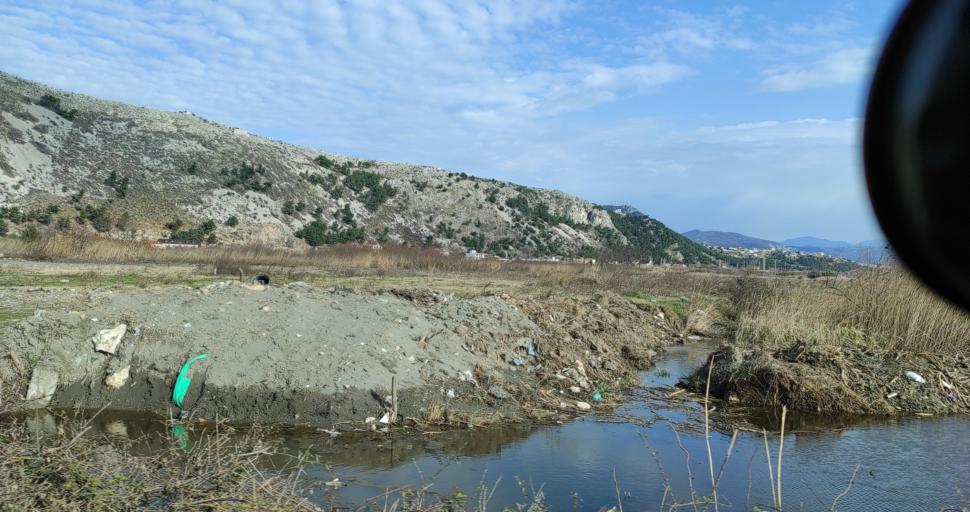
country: AL
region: Lezhe
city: Shengjin
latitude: 41.7975
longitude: 19.6105
